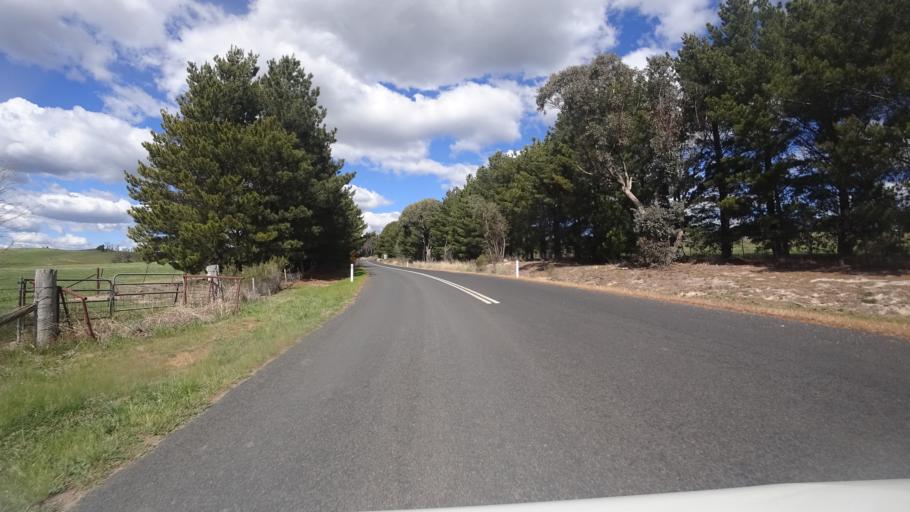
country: AU
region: New South Wales
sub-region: Oberon
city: Oberon
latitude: -33.6689
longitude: 149.7789
